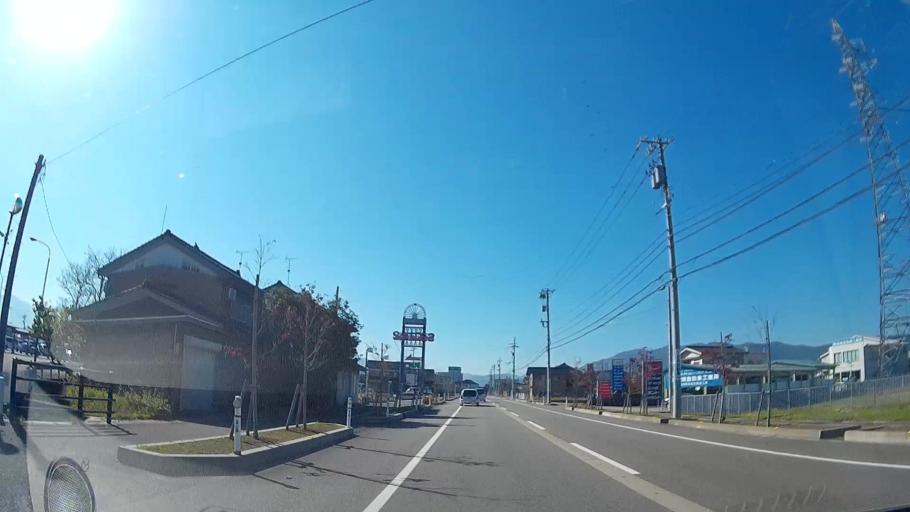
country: JP
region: Toyama
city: Fukumitsu
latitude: 36.5636
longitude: 136.8833
